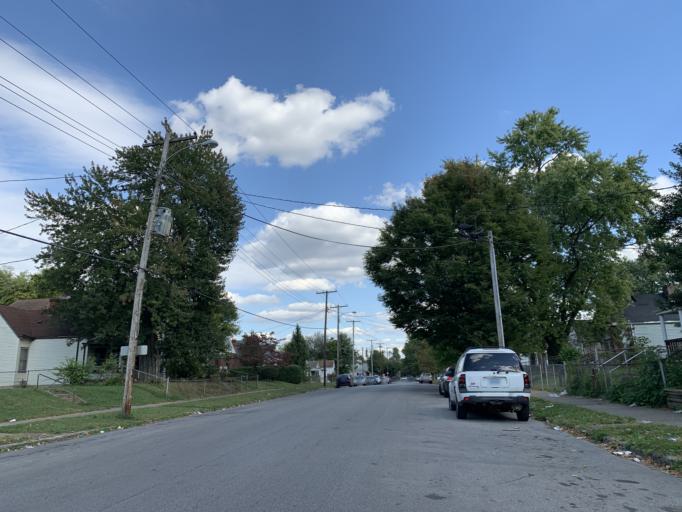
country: US
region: Kentucky
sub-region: Jefferson County
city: Louisville
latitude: 38.2448
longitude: -85.7974
